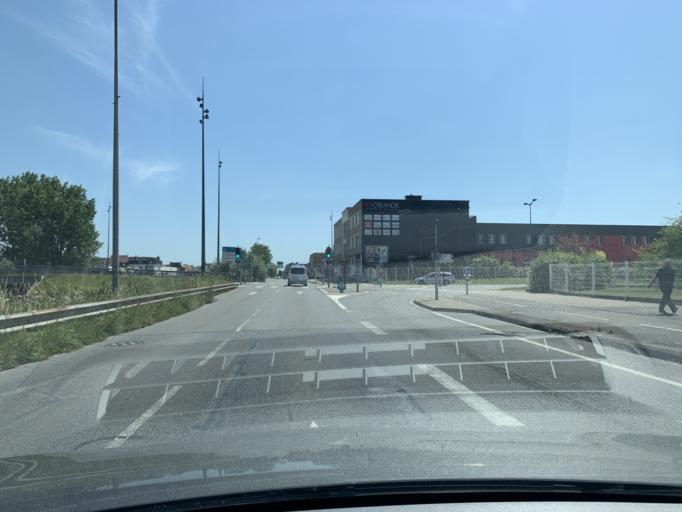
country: FR
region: Nord-Pas-de-Calais
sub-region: Departement du Nord
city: Dunkerque
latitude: 51.0246
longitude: 2.3738
